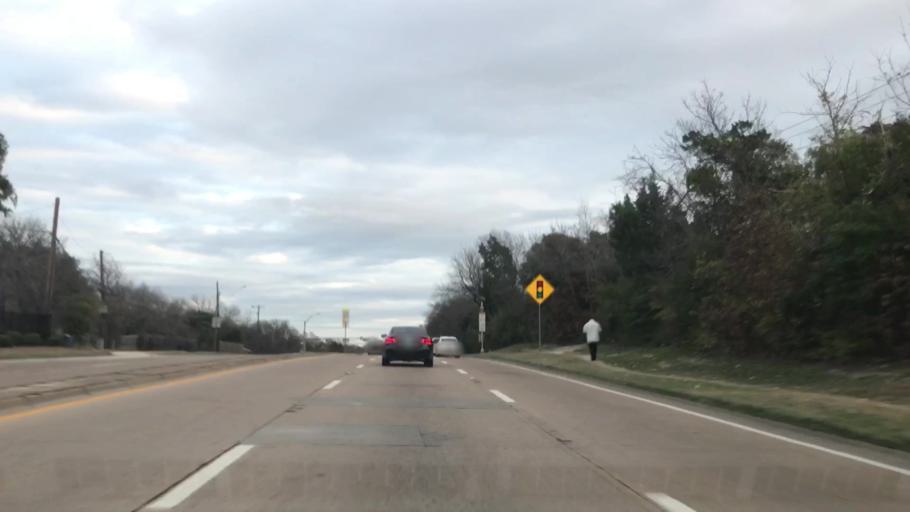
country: US
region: Texas
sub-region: Dallas County
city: Cockrell Hill
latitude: 32.6912
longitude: -96.8542
